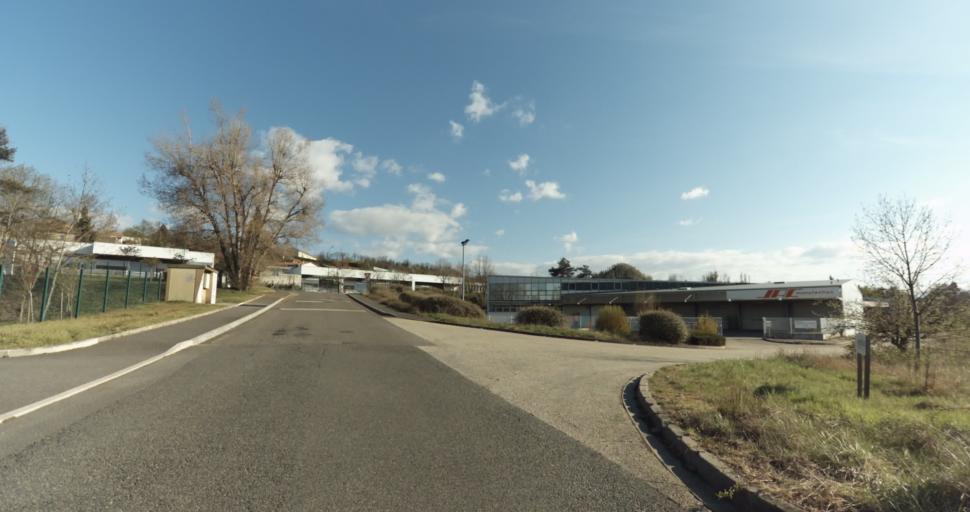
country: FR
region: Rhone-Alpes
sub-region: Departement de la Loire
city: La Talaudiere
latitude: 45.4598
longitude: 4.4241
